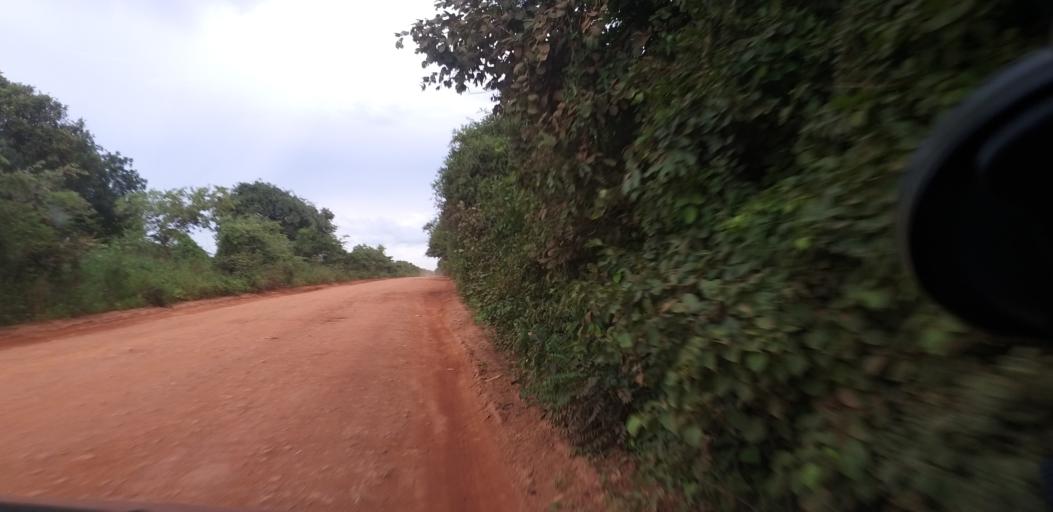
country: ZM
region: Lusaka
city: Lusaka
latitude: -15.2077
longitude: 28.4361
